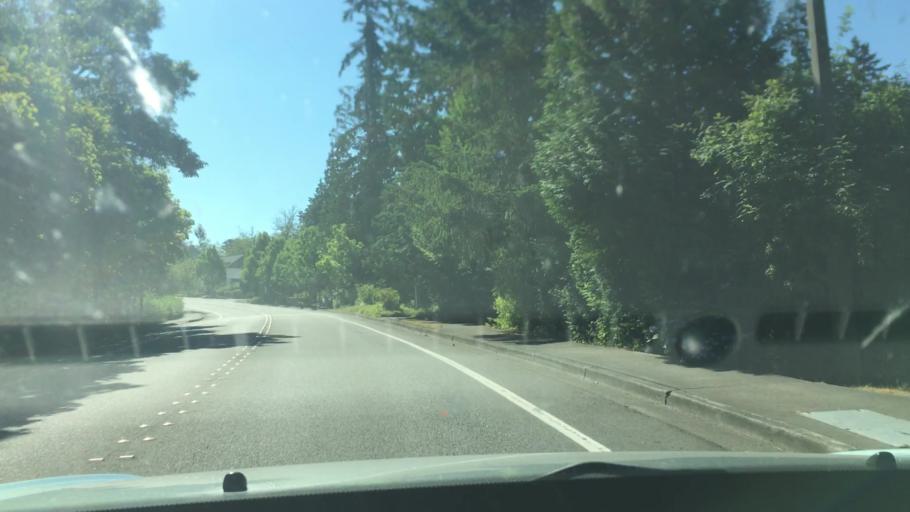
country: US
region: Washington
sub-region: King County
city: Newcastle
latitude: 47.5436
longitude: -122.1265
